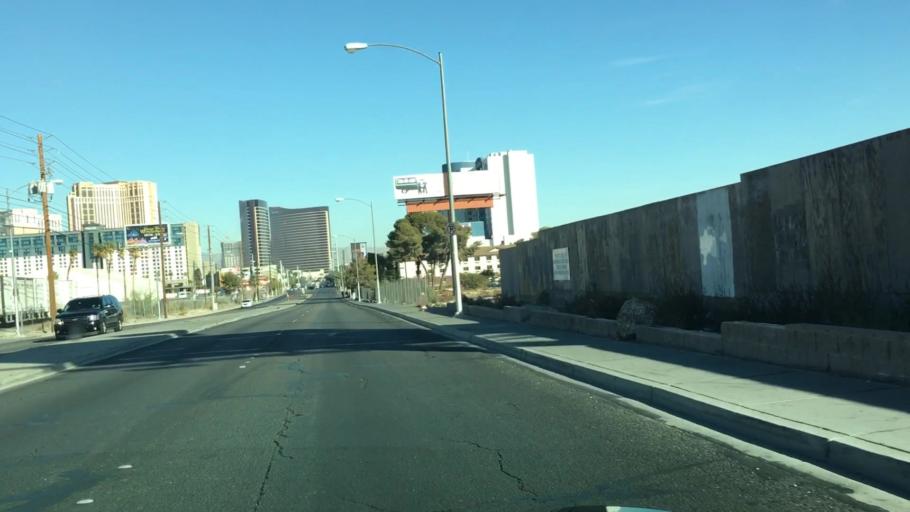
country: US
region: Nevada
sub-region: Clark County
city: Paradise
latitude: 36.1094
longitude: -115.1639
